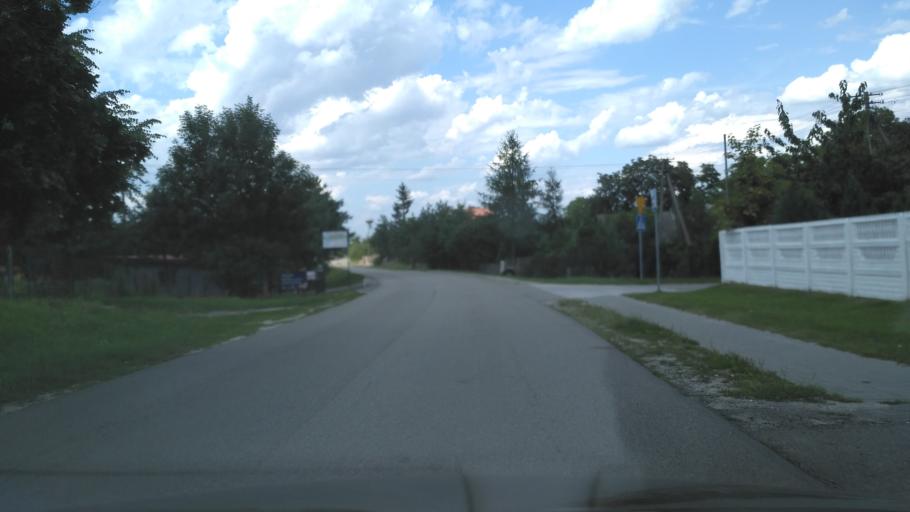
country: PL
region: Lublin Voivodeship
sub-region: Powiat swidnicki
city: Trawniki
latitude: 51.1653
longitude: 22.9795
